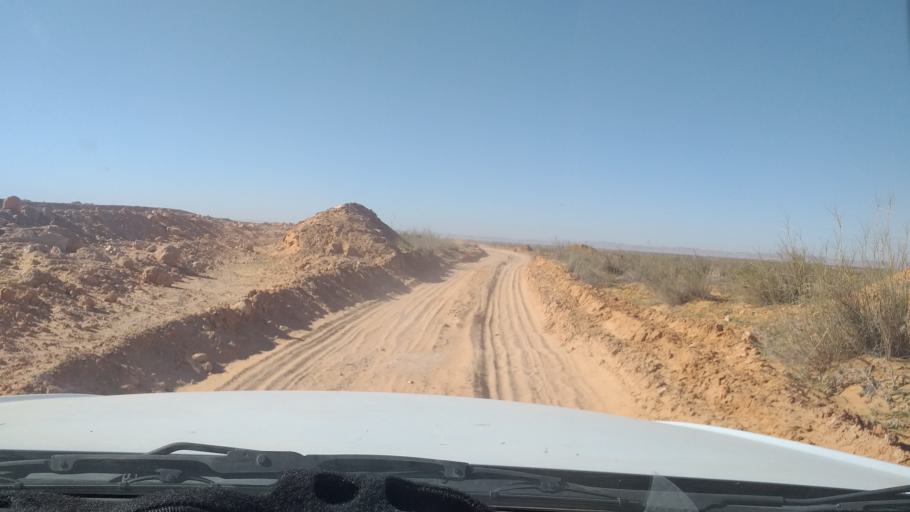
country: TN
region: Madanin
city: Medenine
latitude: 33.2657
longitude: 10.5818
